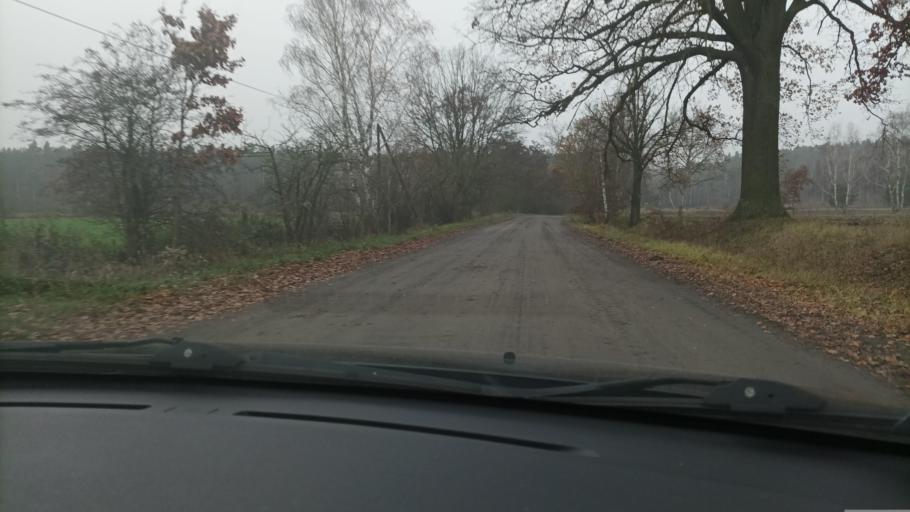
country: PL
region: Greater Poland Voivodeship
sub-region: Powiat obornicki
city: Ryczywol
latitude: 52.7538
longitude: 16.8139
